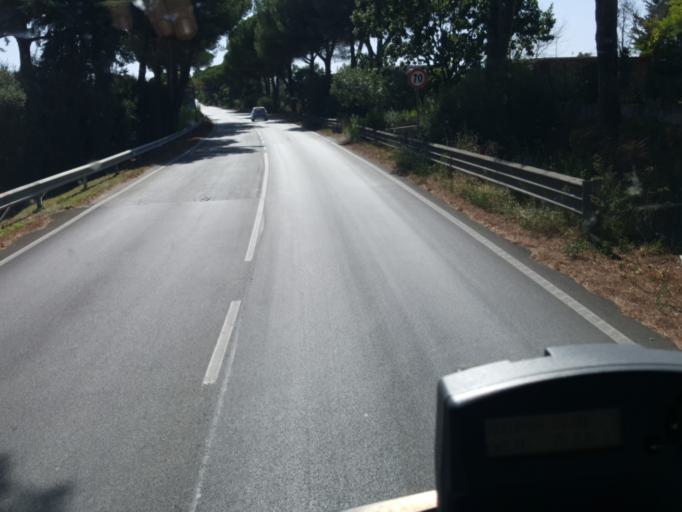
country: IT
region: Latium
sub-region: Provincia di Latina
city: Genio Civile
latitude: 41.5357
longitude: 12.7138
